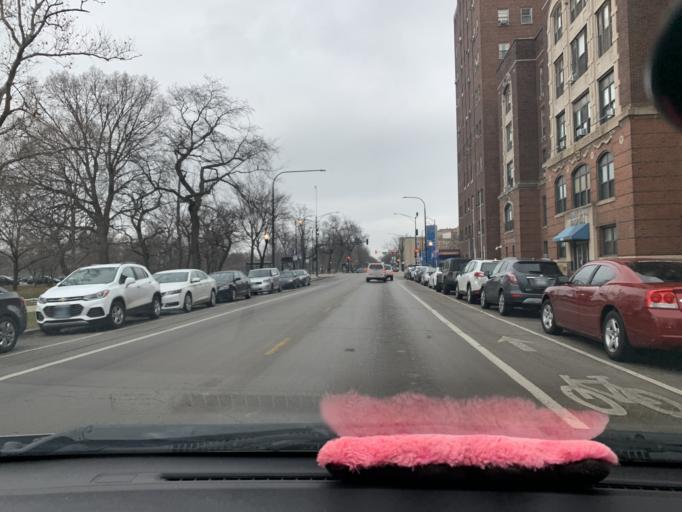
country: US
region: Illinois
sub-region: Cook County
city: Chicago
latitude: 41.8601
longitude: -87.6958
